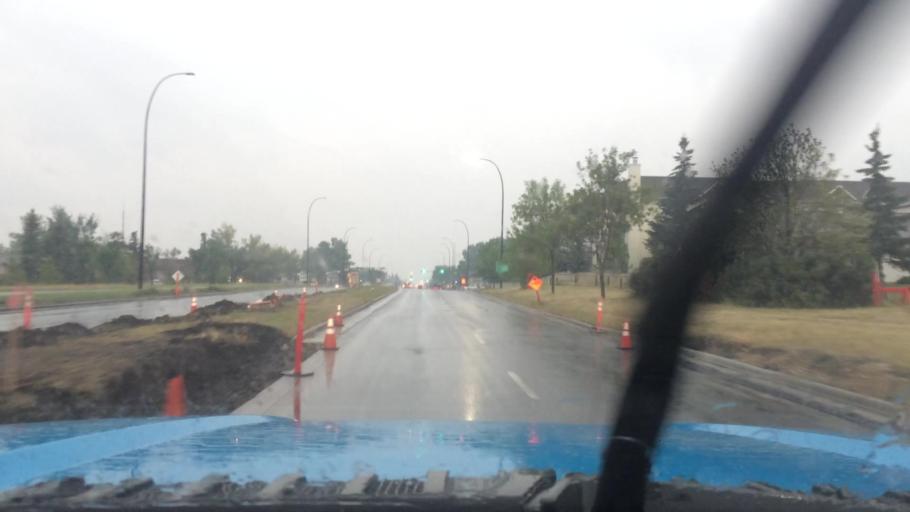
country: CA
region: Alberta
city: Calgary
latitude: 51.0937
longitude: -113.9585
